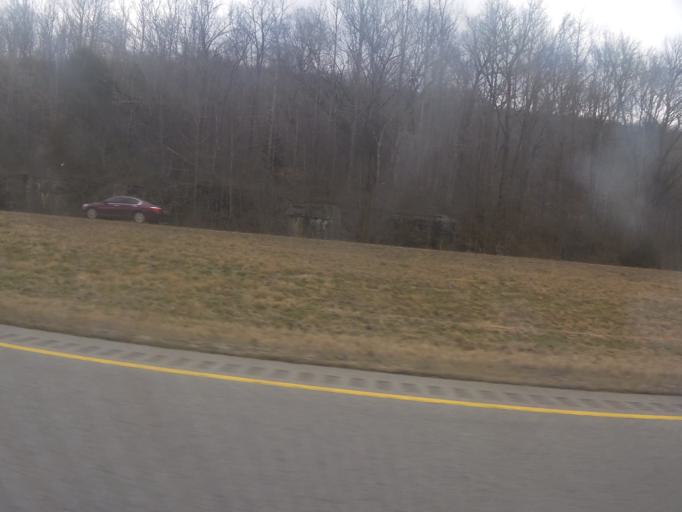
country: US
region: Tennessee
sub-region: Marion County
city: Monteagle
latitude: 35.1351
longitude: -85.7673
